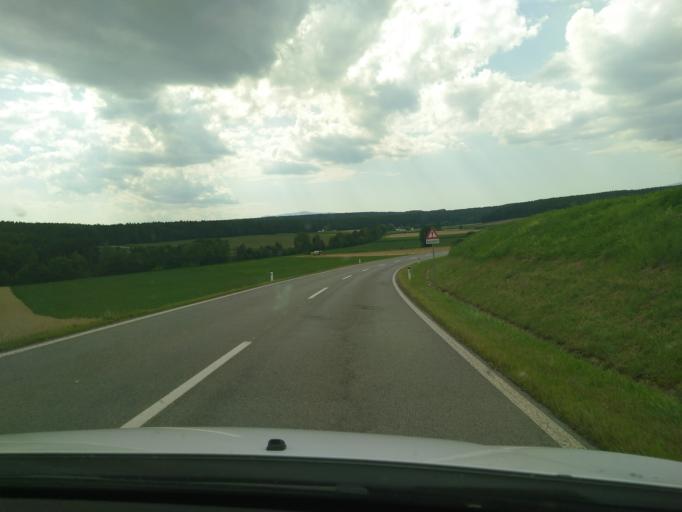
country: AT
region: Burgenland
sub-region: Politischer Bezirk Oberwart
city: Oberschutzen
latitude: 47.3490
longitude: 16.1931
